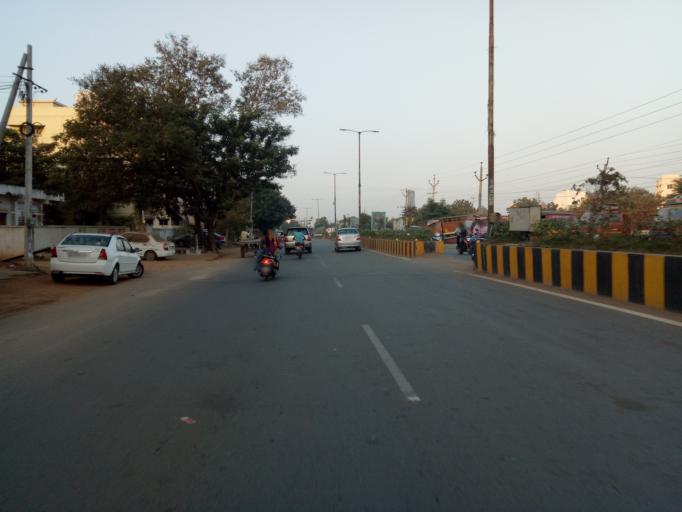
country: IN
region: Andhra Pradesh
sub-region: Nellore
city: Nellore
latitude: 14.4407
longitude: 79.9859
